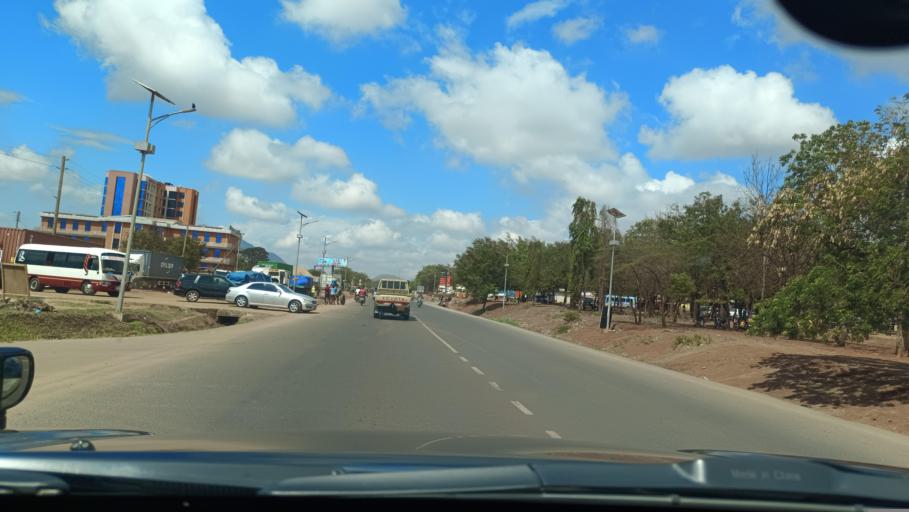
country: TZ
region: Morogoro
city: Morogoro
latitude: -6.8048
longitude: 37.6681
